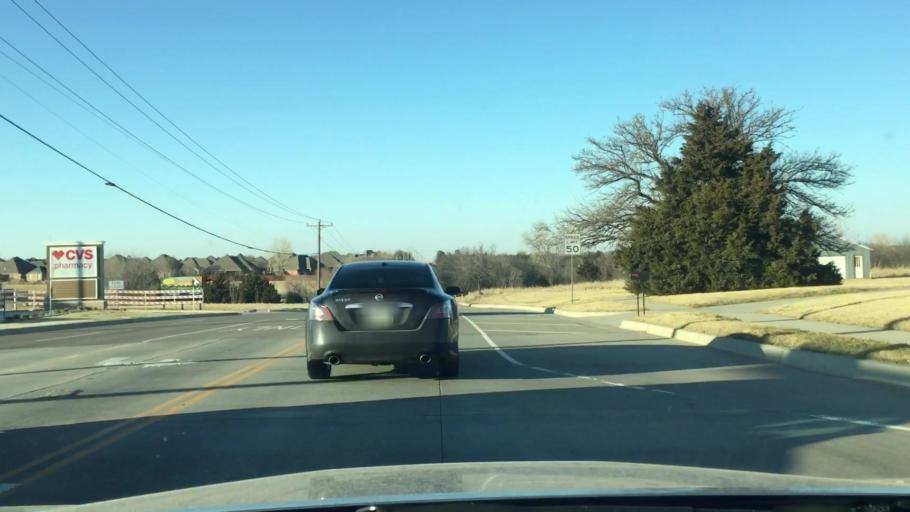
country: US
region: Oklahoma
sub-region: Oklahoma County
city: The Village
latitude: 35.6238
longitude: -97.6208
